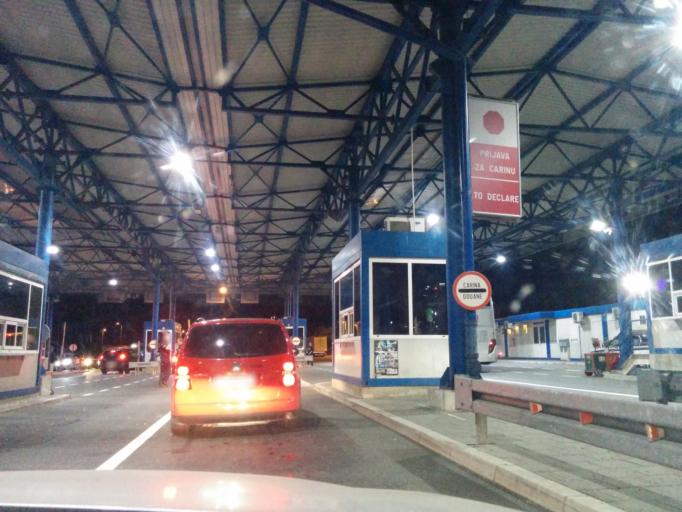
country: HR
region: Vukovarsko-Srijemska
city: Nijemci
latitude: 45.0473
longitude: 19.1073
